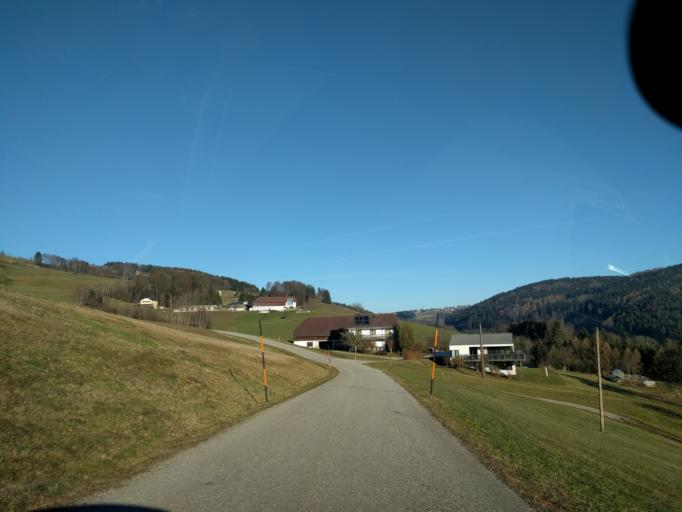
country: AT
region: Upper Austria
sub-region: Politischer Bezirk Urfahr-Umgebung
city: Kirchschlag bei Linz
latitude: 48.3982
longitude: 14.2901
